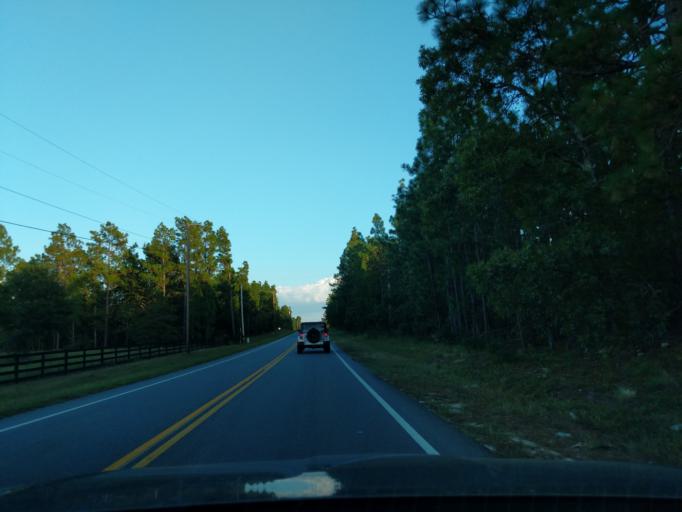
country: US
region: South Carolina
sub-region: Aiken County
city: Burnettown
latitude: 33.5394
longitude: -81.8690
